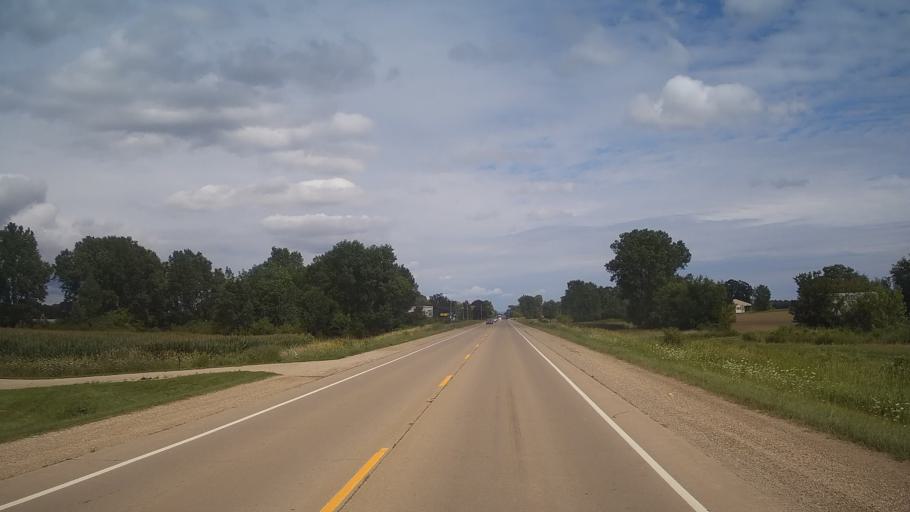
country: US
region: Wisconsin
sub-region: Winnebago County
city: Omro
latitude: 44.0332
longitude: -88.6446
